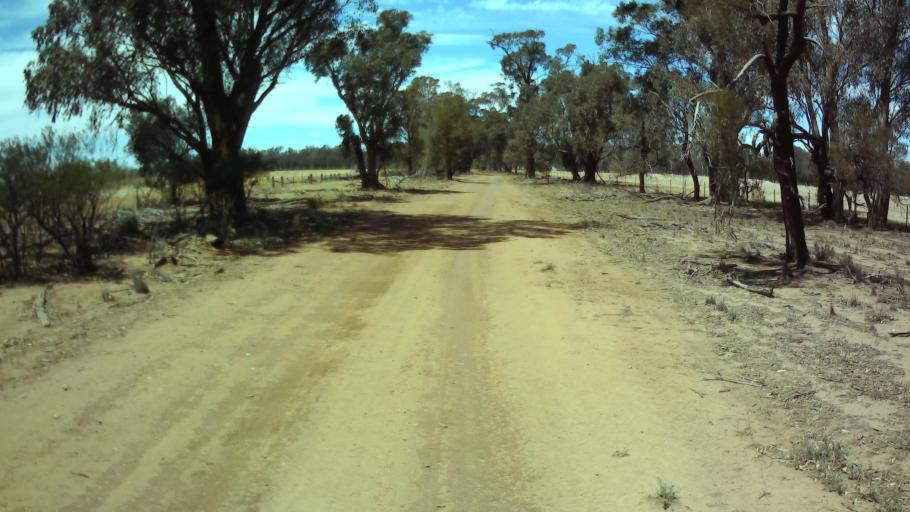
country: AU
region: New South Wales
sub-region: Weddin
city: Grenfell
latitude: -33.9056
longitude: 147.8075
